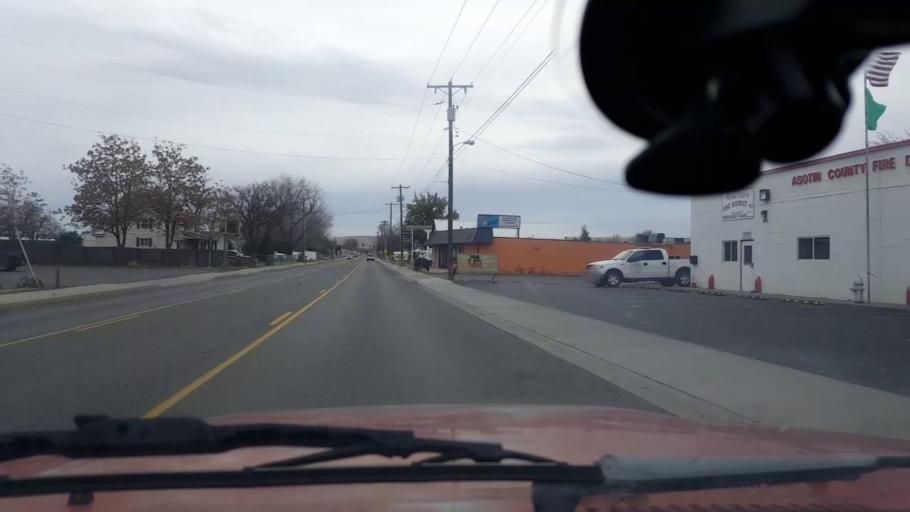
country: US
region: Washington
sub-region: Asotin County
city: Clarkston Heights-Vineland
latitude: 46.3961
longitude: -117.0827
